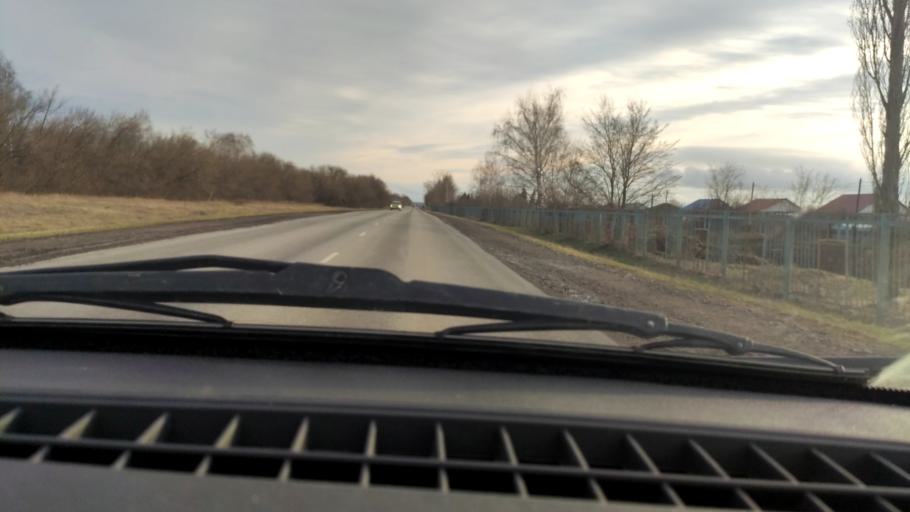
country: RU
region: Bashkortostan
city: Davlekanovo
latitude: 54.2984
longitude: 55.1295
